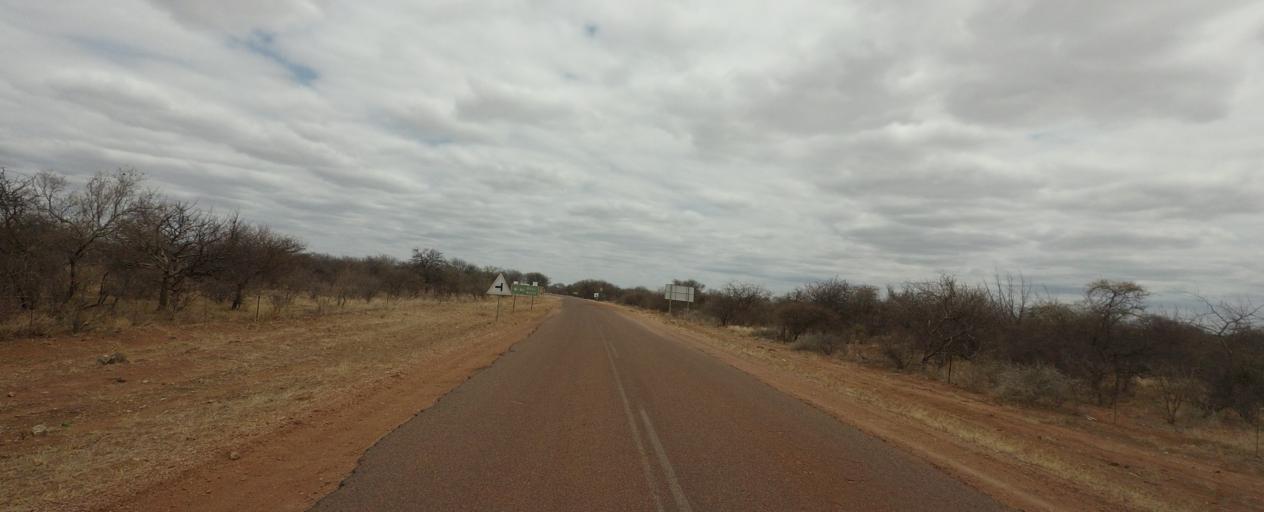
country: BW
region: Central
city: Makobeng
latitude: -22.8463
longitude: 28.2051
